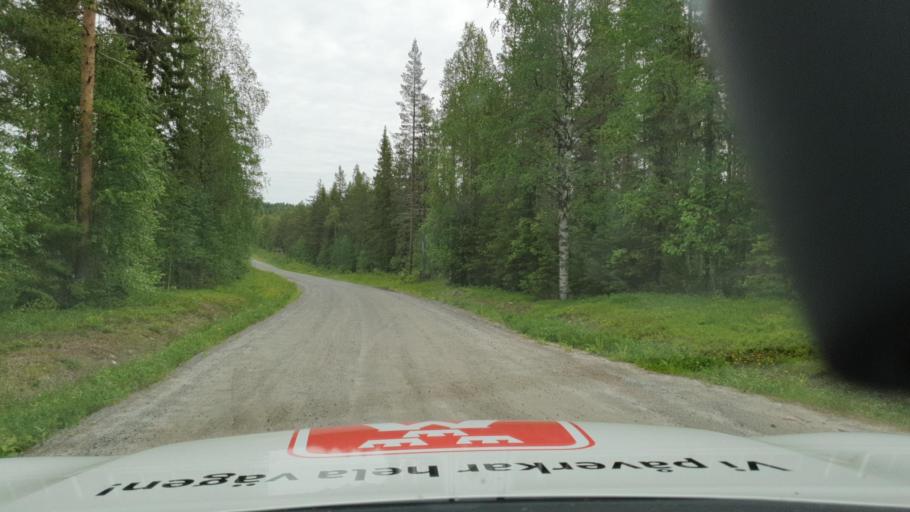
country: SE
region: Vaesterbotten
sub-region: Skelleftea Kommun
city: Langsele
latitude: 64.4770
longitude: 20.2271
